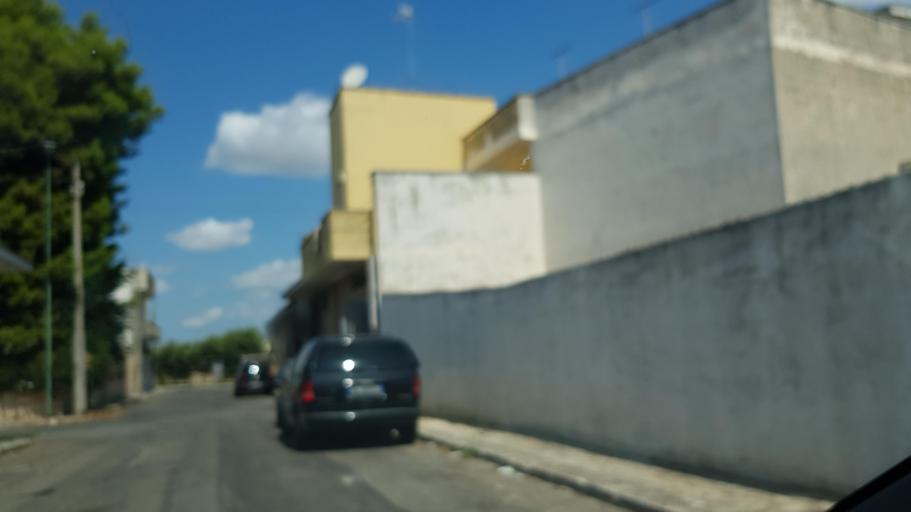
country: IT
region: Apulia
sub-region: Provincia di Lecce
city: Trepuzzi
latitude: 40.4090
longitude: 18.0671
